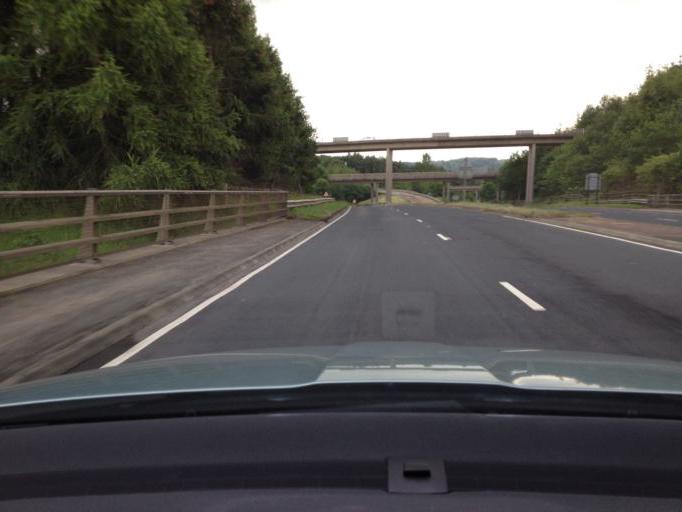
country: GB
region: Scotland
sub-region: Perth and Kinross
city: Perth
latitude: 56.3704
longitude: -3.4233
